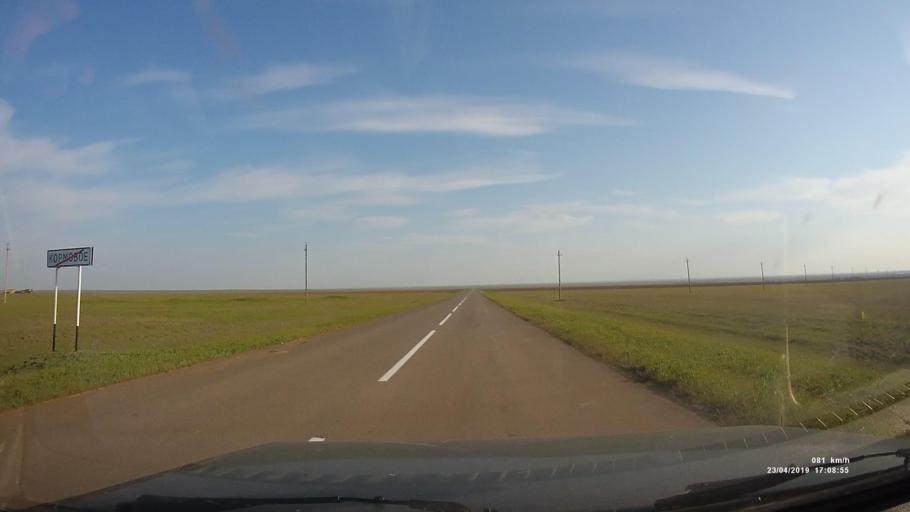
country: RU
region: Kalmykiya
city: Priyutnoye
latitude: 46.2654
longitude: 43.4844
